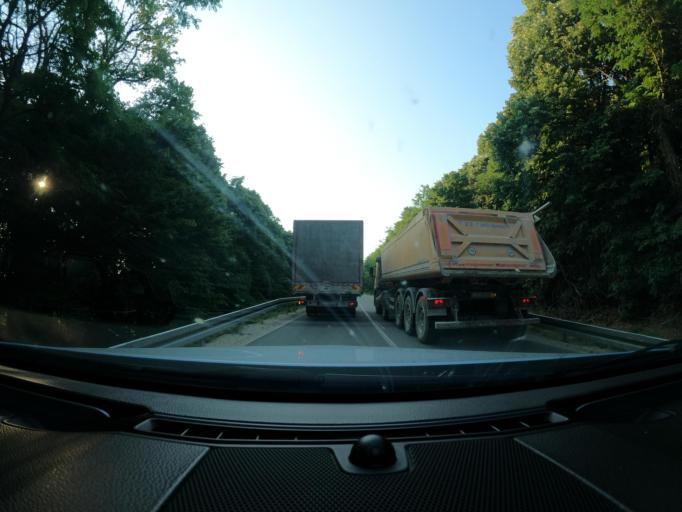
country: RS
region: Autonomna Pokrajina Vojvodina
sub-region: Juznobacki Okrug
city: Beocin
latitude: 45.1409
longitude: 19.7212
